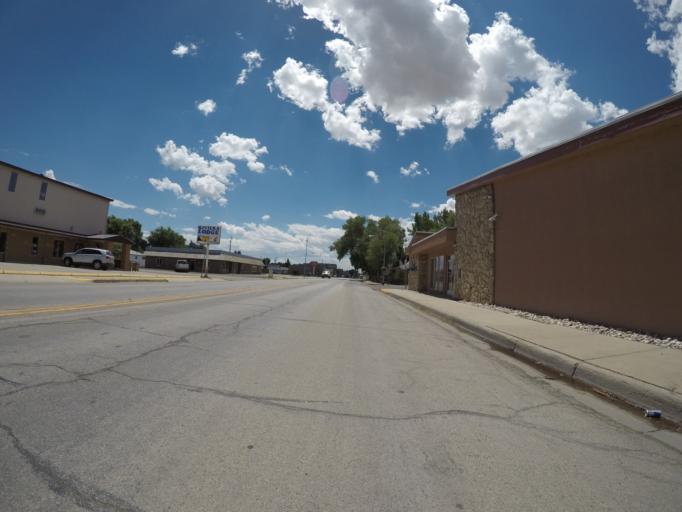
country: US
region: Wyoming
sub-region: Carbon County
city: Saratoga
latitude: 41.4570
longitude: -106.8077
